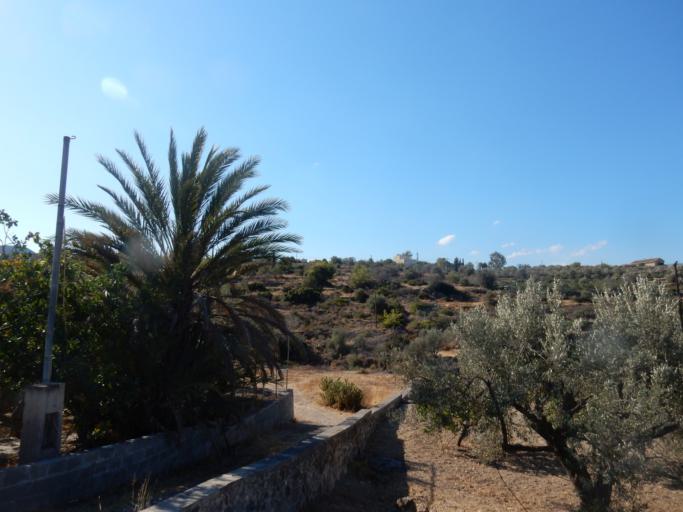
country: GR
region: Attica
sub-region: Nomos Piraios
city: Kypseli
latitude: 37.7348
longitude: 23.4542
